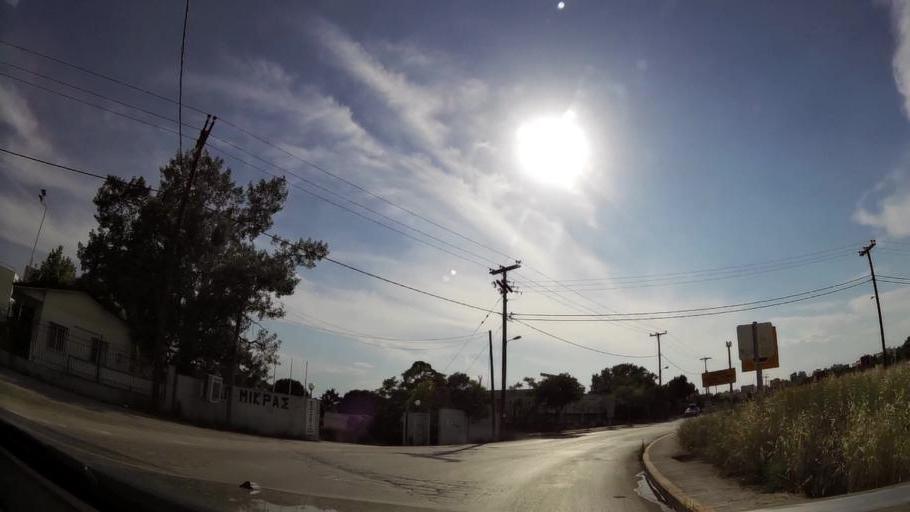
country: GR
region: Central Macedonia
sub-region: Nomos Thessalonikis
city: Kalamaria
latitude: 40.5658
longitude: 22.9677
